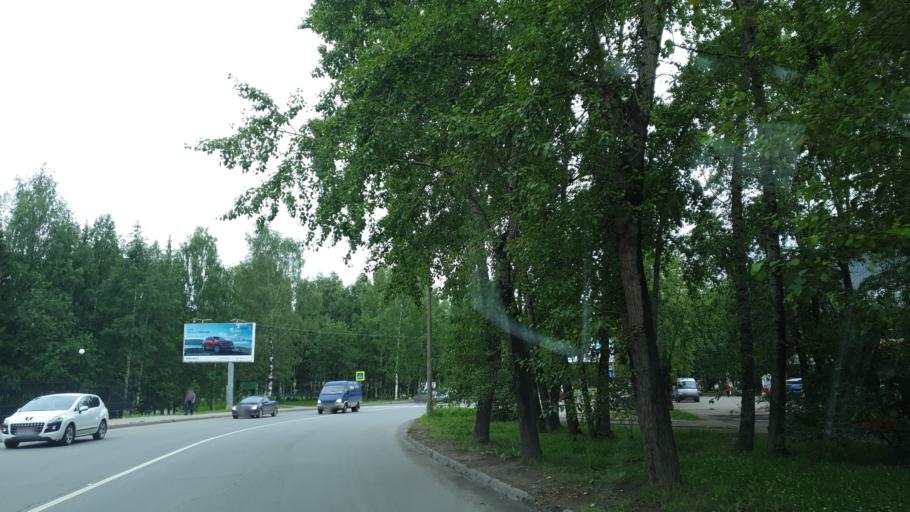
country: RU
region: Komi Republic
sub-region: Syktyvdinskiy Rayon
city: Syktyvkar
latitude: 61.6598
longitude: 50.8213
